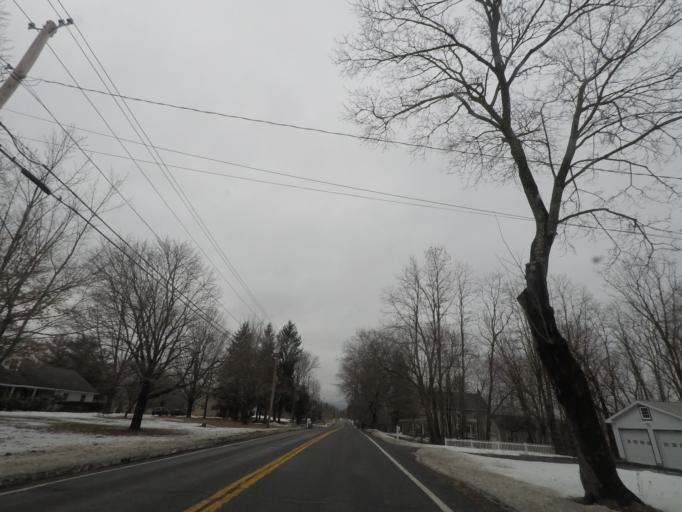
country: US
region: New York
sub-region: Albany County
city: Voorheesville
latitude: 42.6527
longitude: -73.9542
